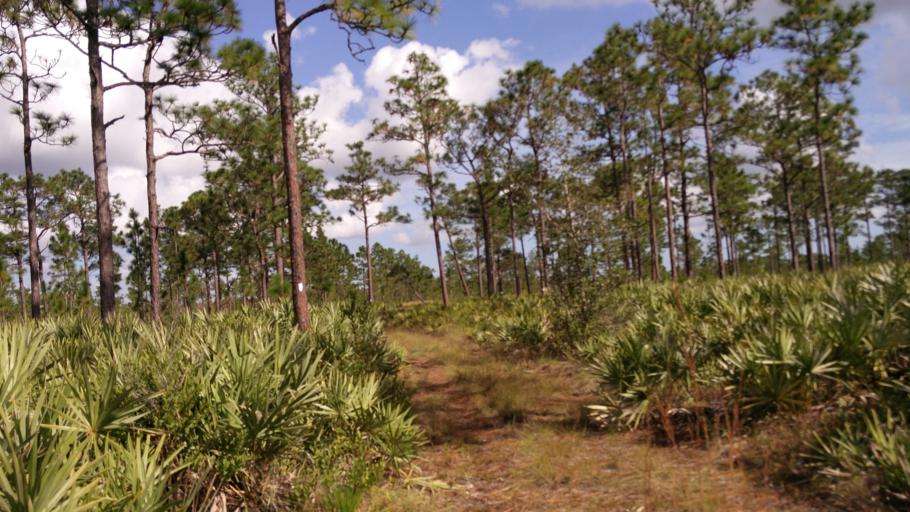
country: US
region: Florida
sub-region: Brevard County
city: June Park
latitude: 28.0493
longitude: -80.9659
